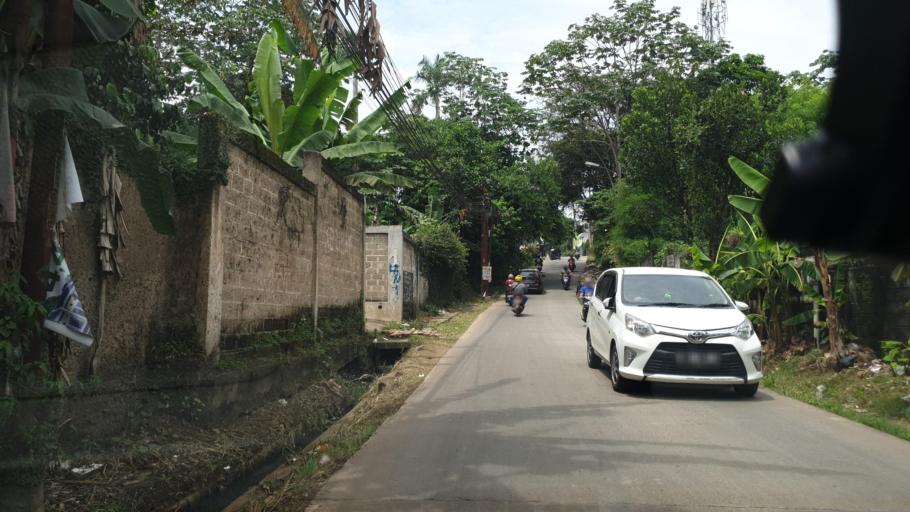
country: ID
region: West Java
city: Pamulang
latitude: -6.3664
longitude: 106.7518
